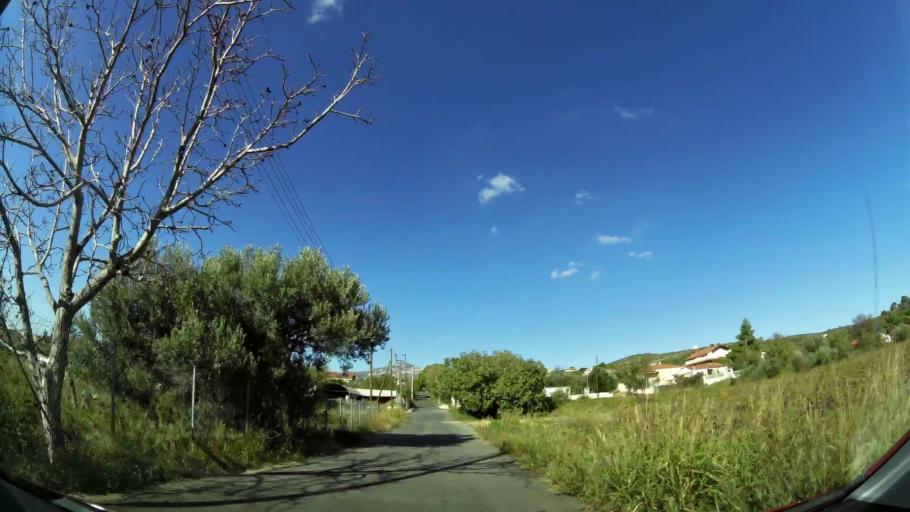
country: GR
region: Attica
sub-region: Nomarchia Anatolikis Attikis
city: Anthousa
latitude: 38.0123
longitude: 23.8764
